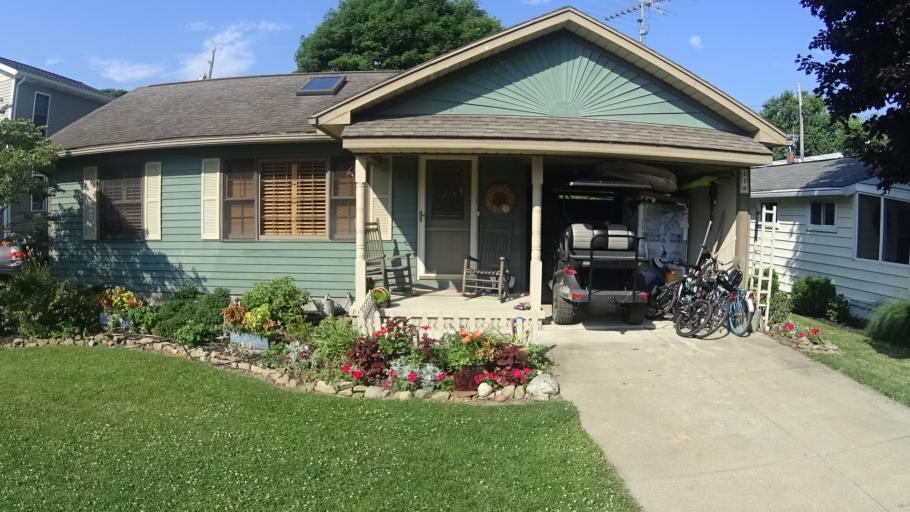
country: US
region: Ohio
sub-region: Lorain County
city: Vermilion
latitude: 41.3920
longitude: -82.4418
